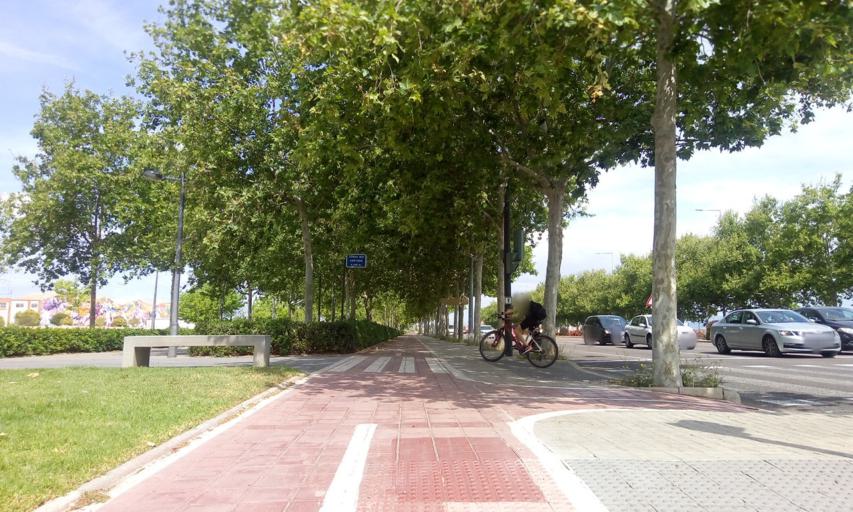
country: ES
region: Valencia
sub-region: Provincia de Valencia
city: Tavernes Blanques
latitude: 39.4998
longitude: -0.3890
